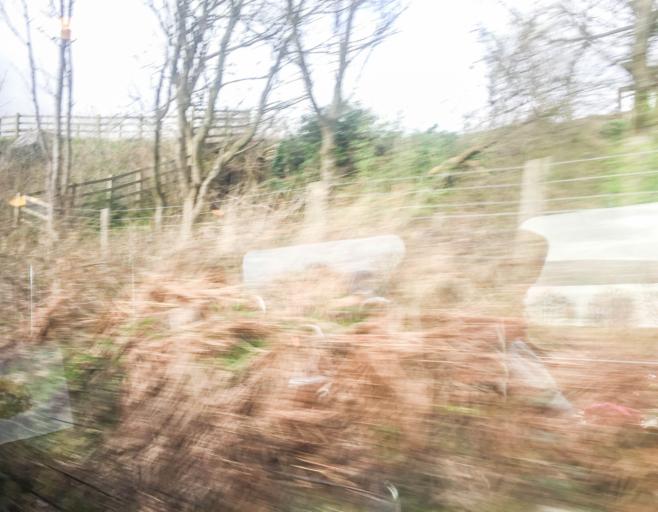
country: GB
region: Scotland
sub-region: Argyll and Bute
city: Cardross
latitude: 55.9504
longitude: -4.6183
